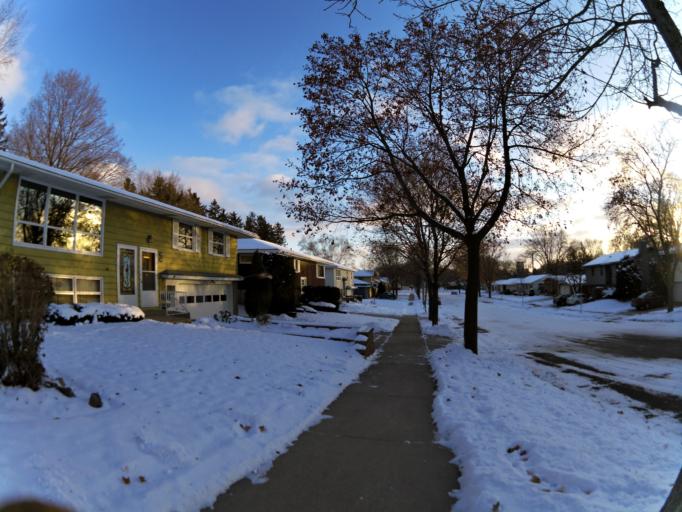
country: US
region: Minnesota
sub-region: Olmsted County
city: Rochester
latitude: 44.0383
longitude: -92.4556
